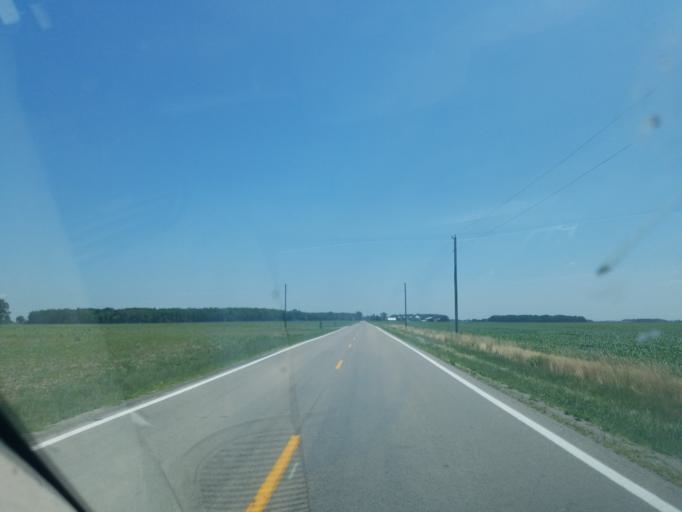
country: US
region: Ohio
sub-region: Allen County
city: Spencerville
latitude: 40.7429
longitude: -84.4303
